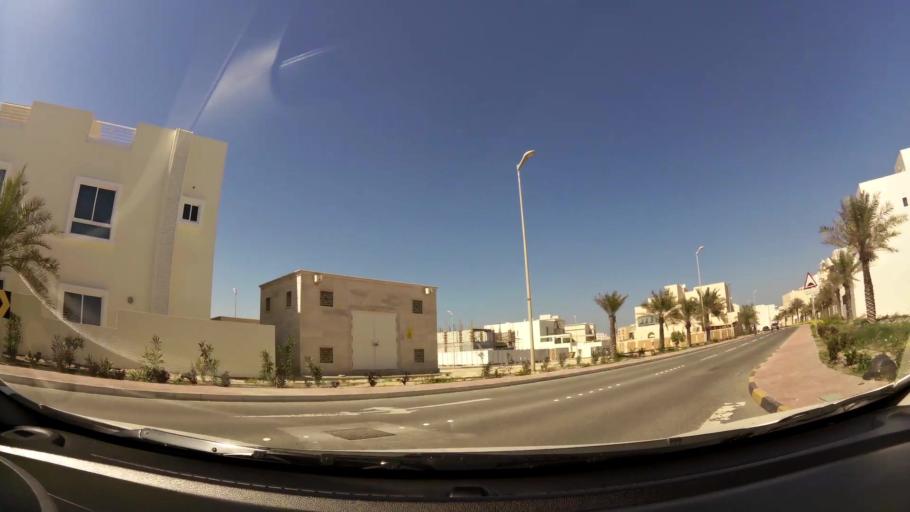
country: BH
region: Muharraq
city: Al Hadd
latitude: 26.2886
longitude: 50.6739
